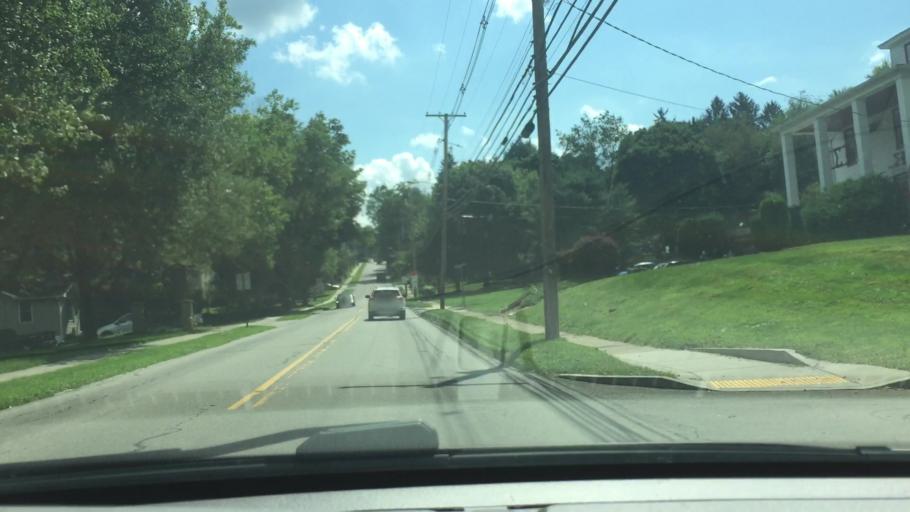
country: US
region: Pennsylvania
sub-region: Lawrence County
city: New Wilmington
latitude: 41.1181
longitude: -80.3354
